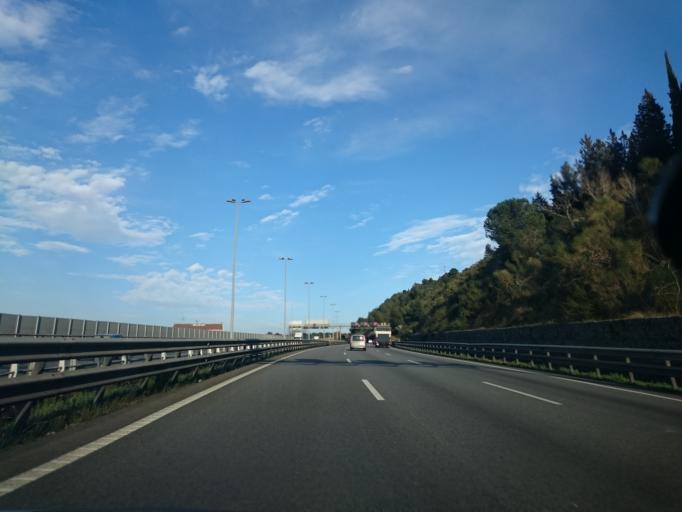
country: ES
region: Catalonia
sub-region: Provincia de Barcelona
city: Martorell
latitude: 41.4714
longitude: 1.9268
